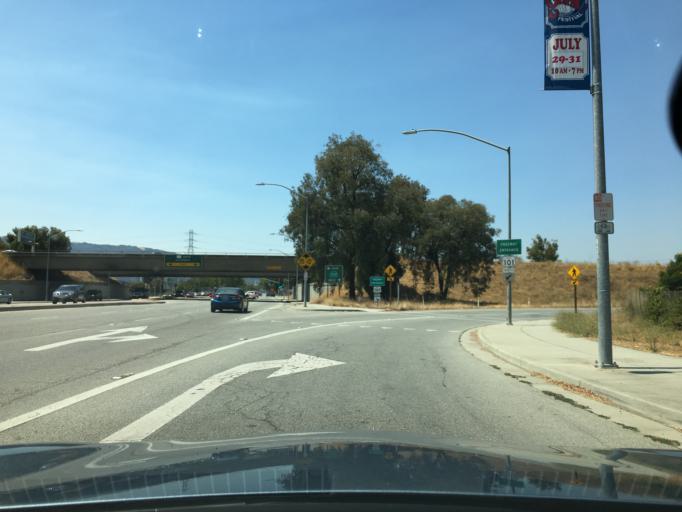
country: US
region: California
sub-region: Santa Clara County
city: Gilroy
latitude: 37.0230
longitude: -121.5653
